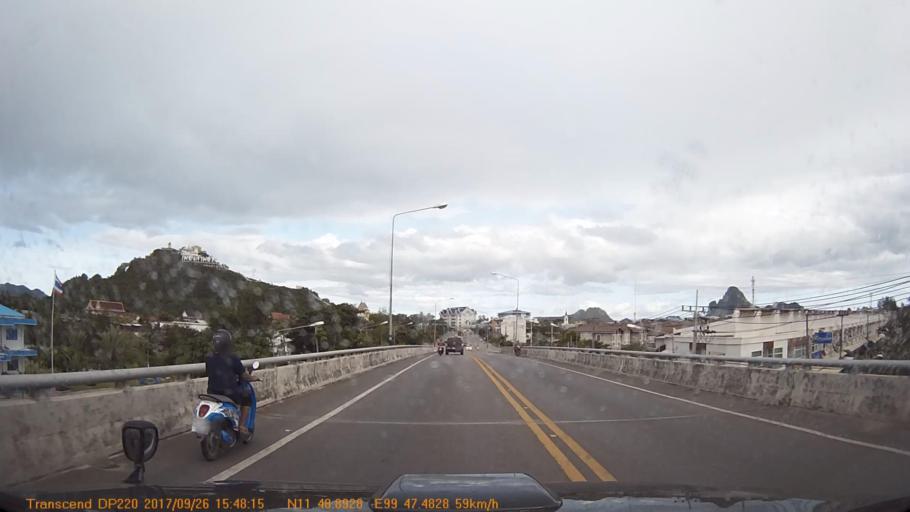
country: TH
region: Prachuap Khiri Khan
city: Prachuap Khiri Khan
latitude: 11.8148
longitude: 99.7916
